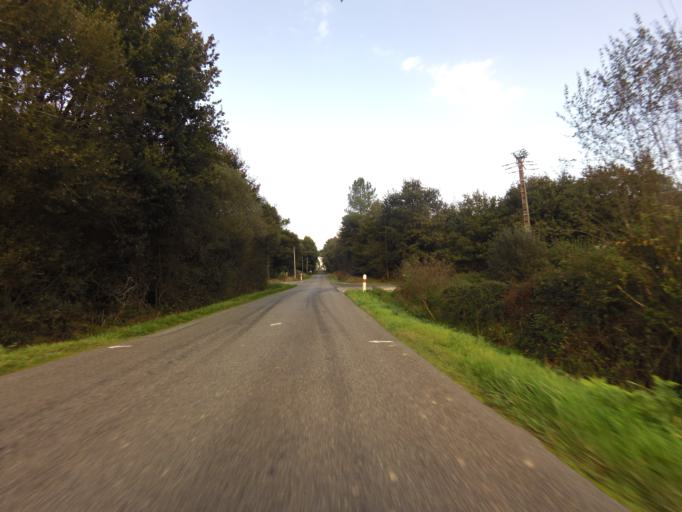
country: FR
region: Brittany
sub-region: Departement du Morbihan
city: Pleucadeuc
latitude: 47.7542
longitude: -2.3845
